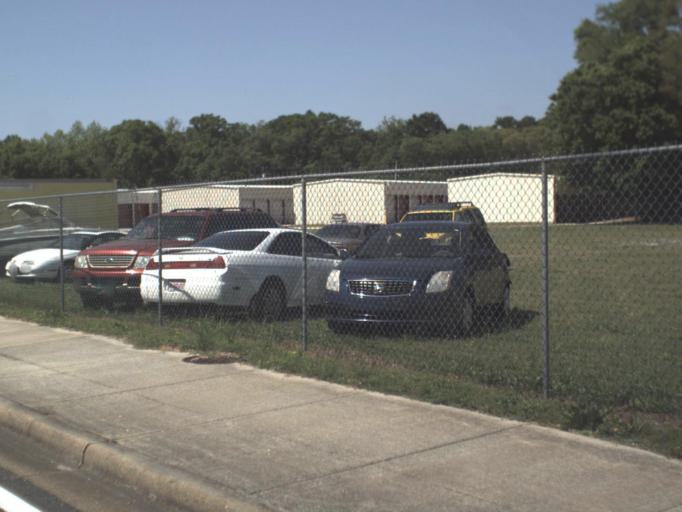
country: US
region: Florida
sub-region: Escambia County
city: Brent
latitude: 30.4565
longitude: -87.2403
